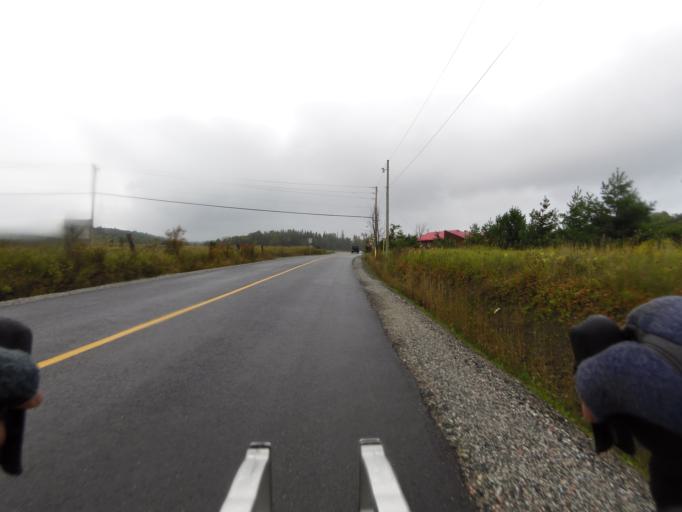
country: CA
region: Quebec
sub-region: Outaouais
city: Wakefield
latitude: 45.6438
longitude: -75.8902
